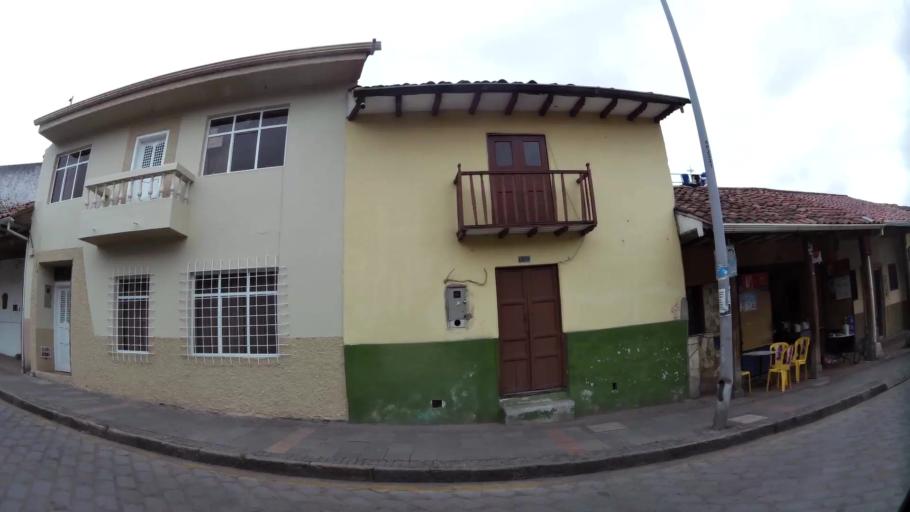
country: EC
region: Azuay
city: Cuenca
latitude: -2.9039
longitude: -79.0228
